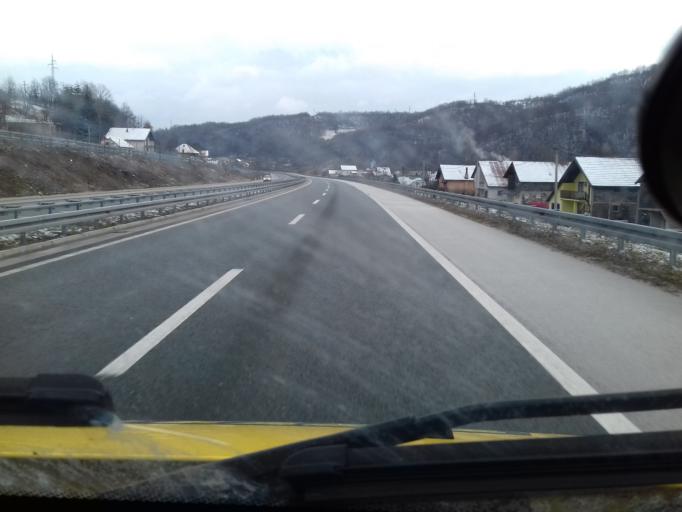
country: BA
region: Federation of Bosnia and Herzegovina
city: Kakanj
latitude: 44.1333
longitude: 18.0542
